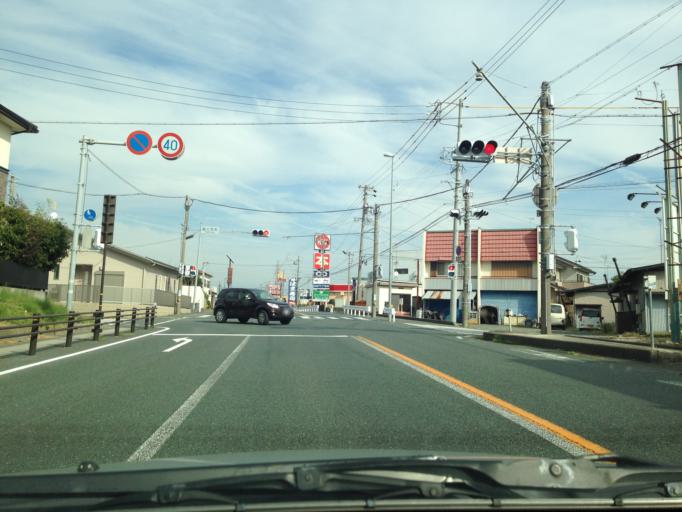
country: JP
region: Shizuoka
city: Iwata
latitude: 34.7277
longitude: 137.8674
